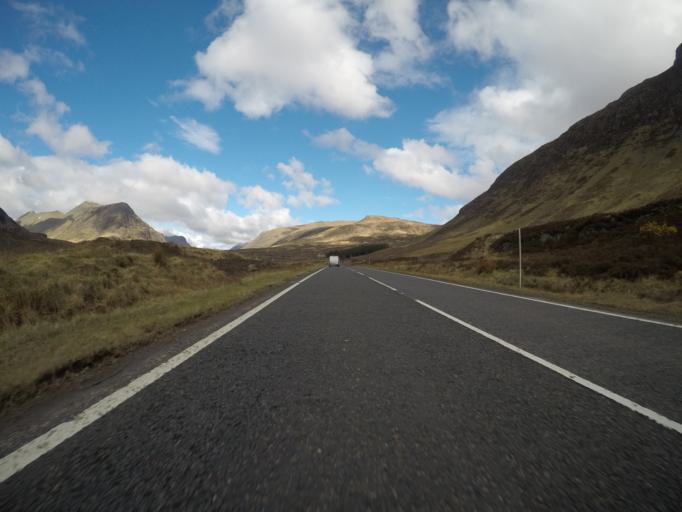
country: GB
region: Scotland
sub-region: Highland
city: Spean Bridge
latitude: 56.6613
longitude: -4.8910
